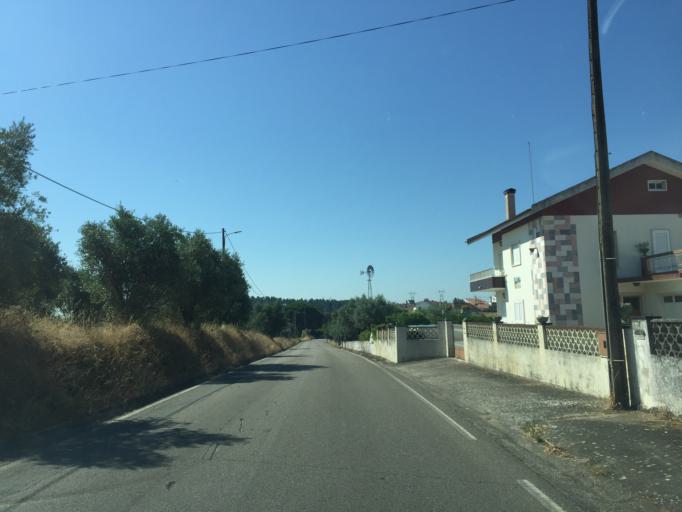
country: PT
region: Santarem
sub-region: Tomar
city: Tomar
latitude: 39.5786
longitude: -8.3250
